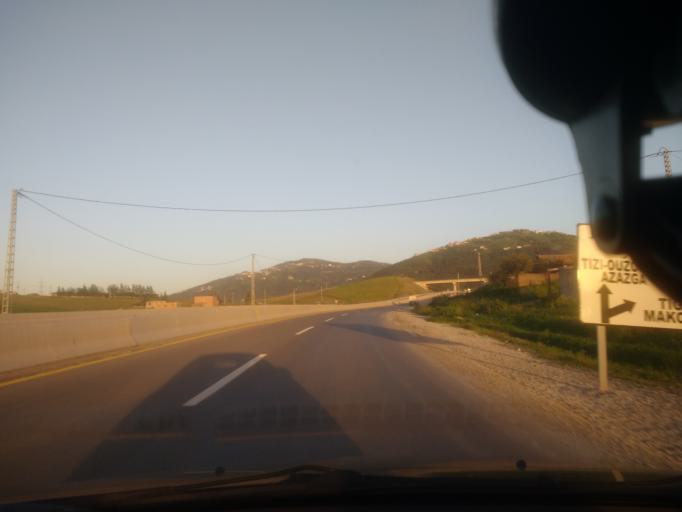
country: DZ
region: Boumerdes
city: Makouda
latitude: 36.7576
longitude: 4.0476
